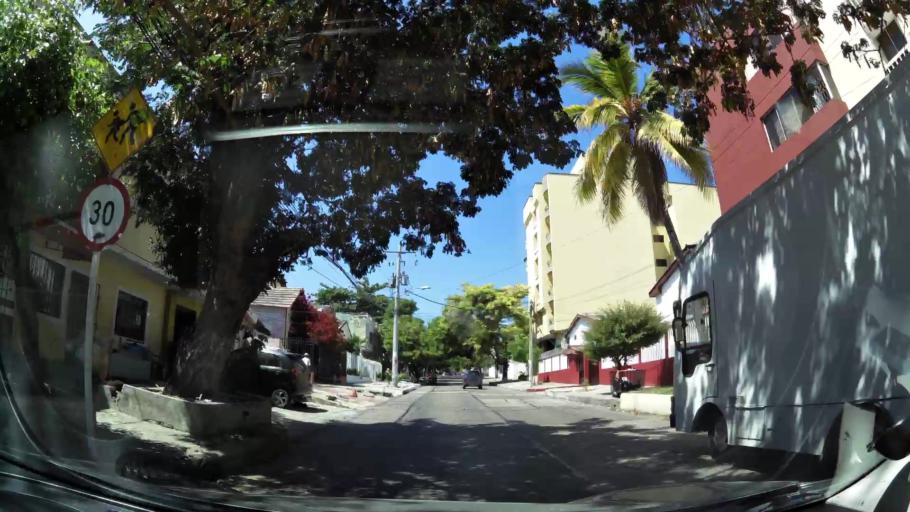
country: CO
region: Atlantico
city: Barranquilla
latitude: 10.9904
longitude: -74.7997
